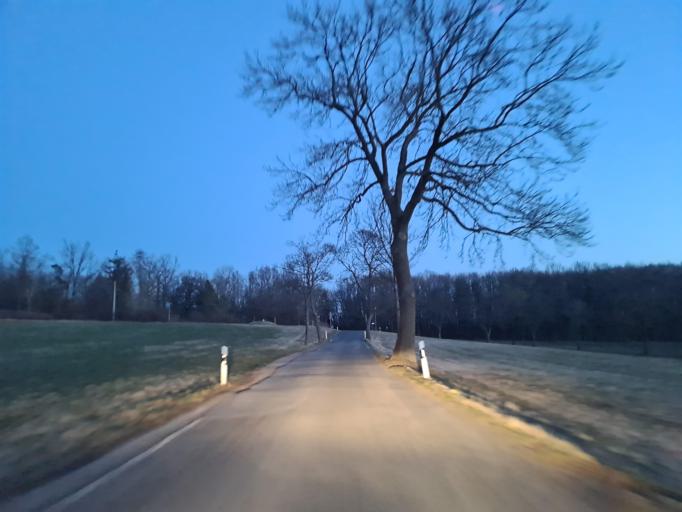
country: DE
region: Saxony
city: Plauen
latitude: 50.5151
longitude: 12.1104
